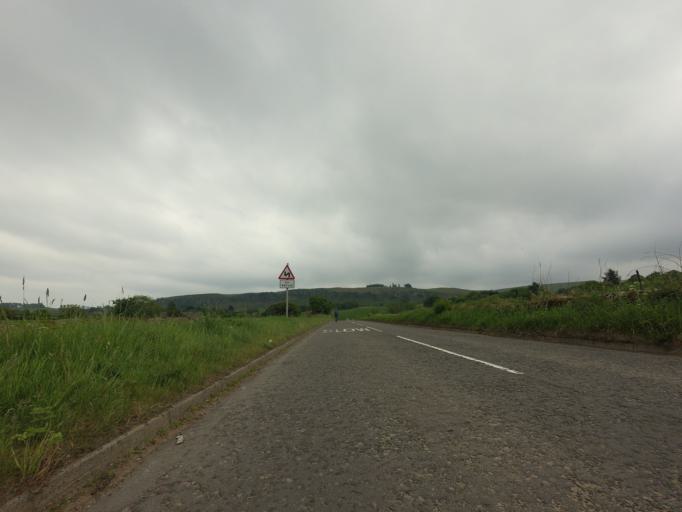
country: GB
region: Scotland
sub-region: Perth and Kinross
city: Kinross
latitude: 56.1661
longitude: -3.4474
